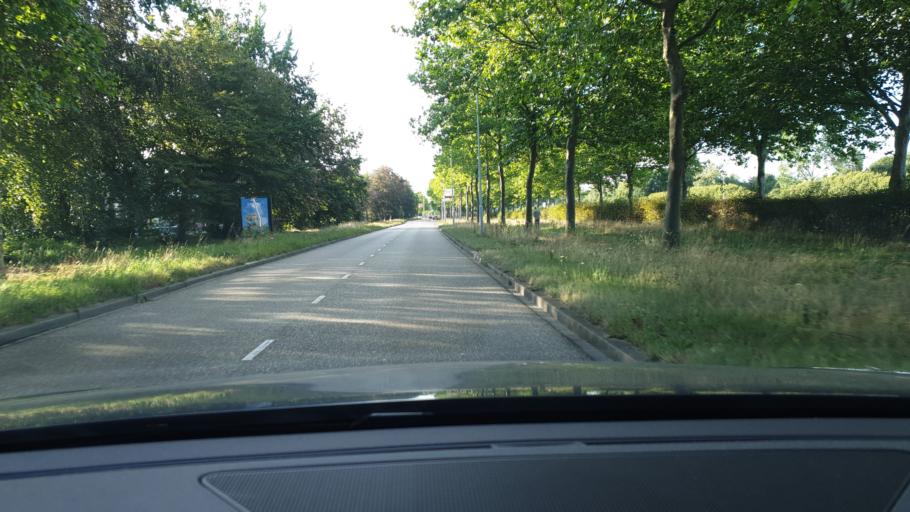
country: NL
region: North Brabant
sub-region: Gemeente Best
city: Best
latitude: 51.5124
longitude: 5.4039
